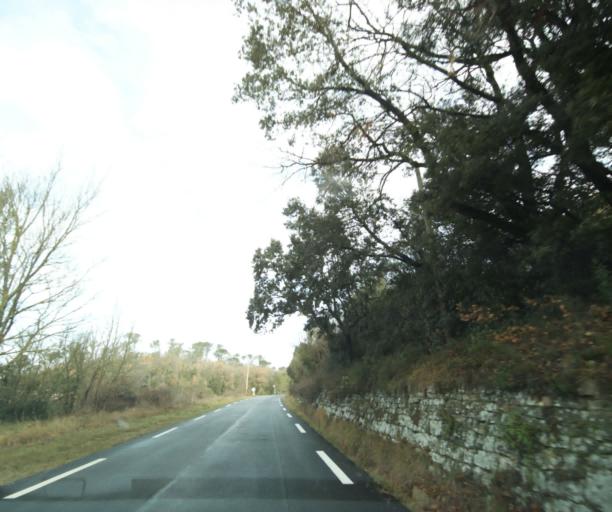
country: FR
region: Provence-Alpes-Cote d'Azur
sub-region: Departement du Var
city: Tourves
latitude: 43.4157
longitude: 5.9260
